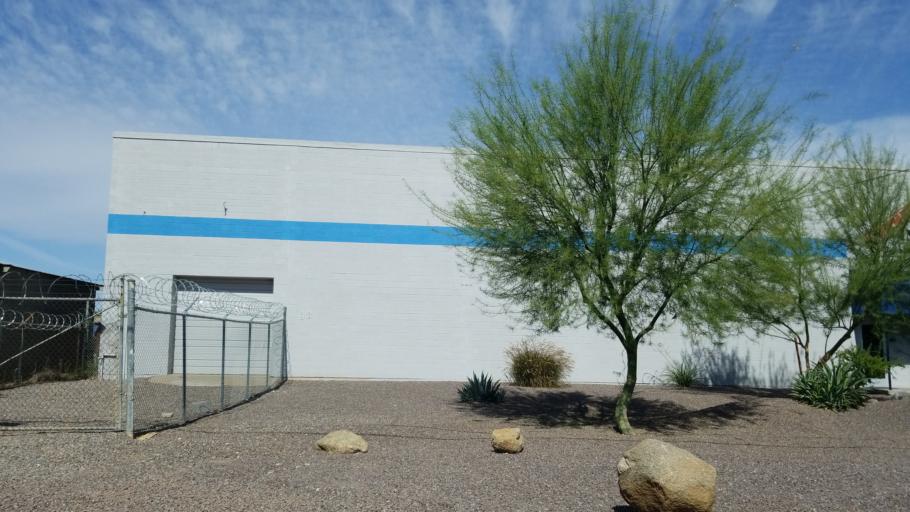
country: US
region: Arizona
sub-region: Maricopa County
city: Phoenix
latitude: 33.4591
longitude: -112.1060
